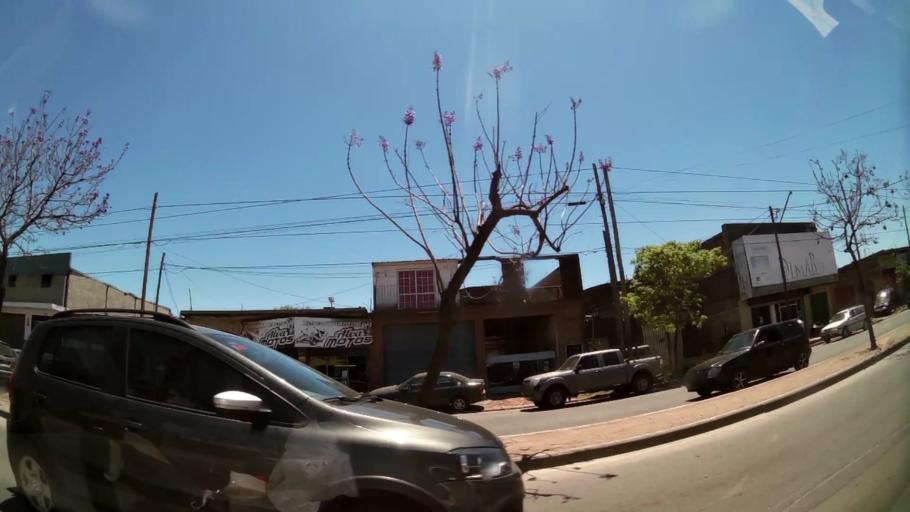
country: AR
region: Buenos Aires
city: Hurlingham
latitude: -34.5034
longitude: -58.7159
